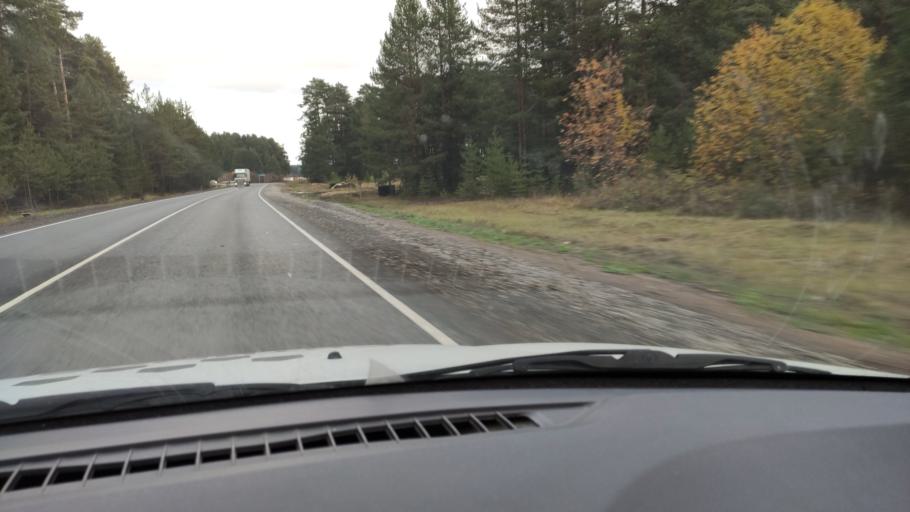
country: RU
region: Kirov
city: Belaya Kholunitsa
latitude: 58.8574
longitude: 50.8403
